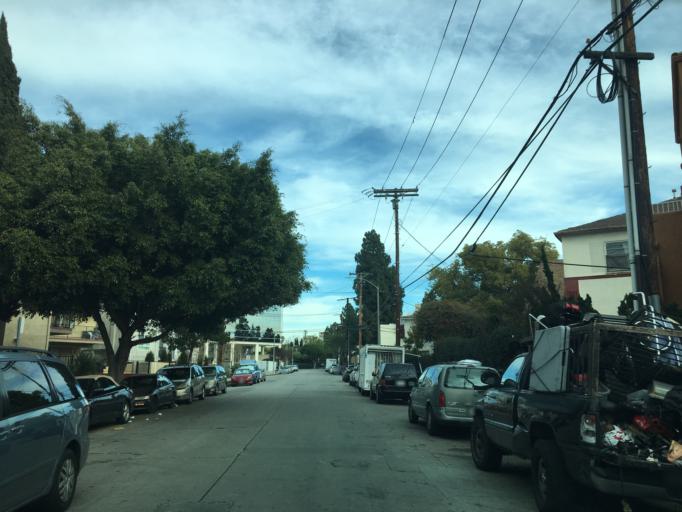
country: US
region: California
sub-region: Los Angeles County
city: Echo Park
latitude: 34.0628
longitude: -118.2765
